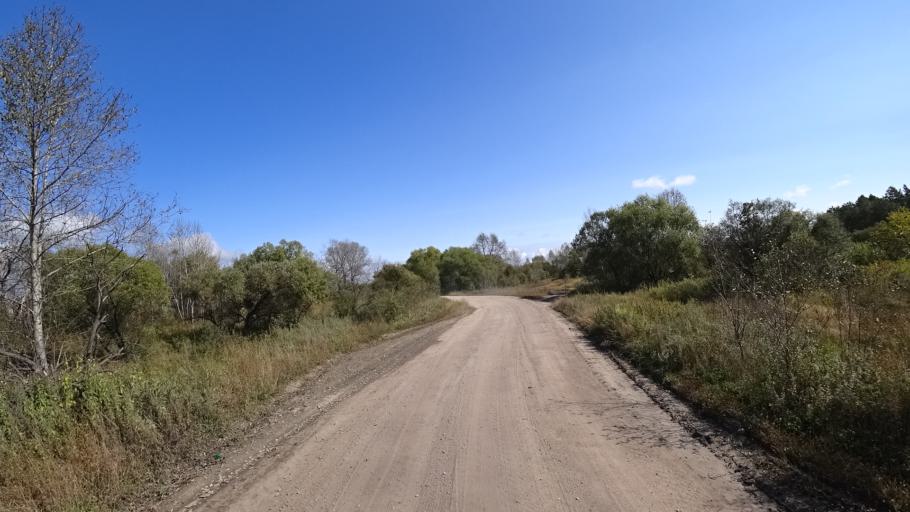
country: RU
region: Amur
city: Arkhara
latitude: 49.4073
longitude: 130.1586
